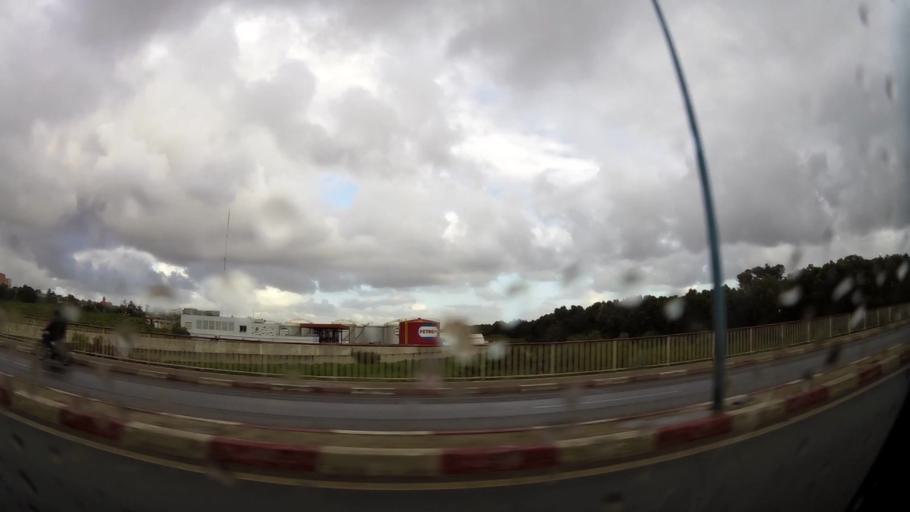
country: MA
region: Grand Casablanca
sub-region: Mohammedia
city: Mohammedia
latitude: 33.6791
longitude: -7.4108
